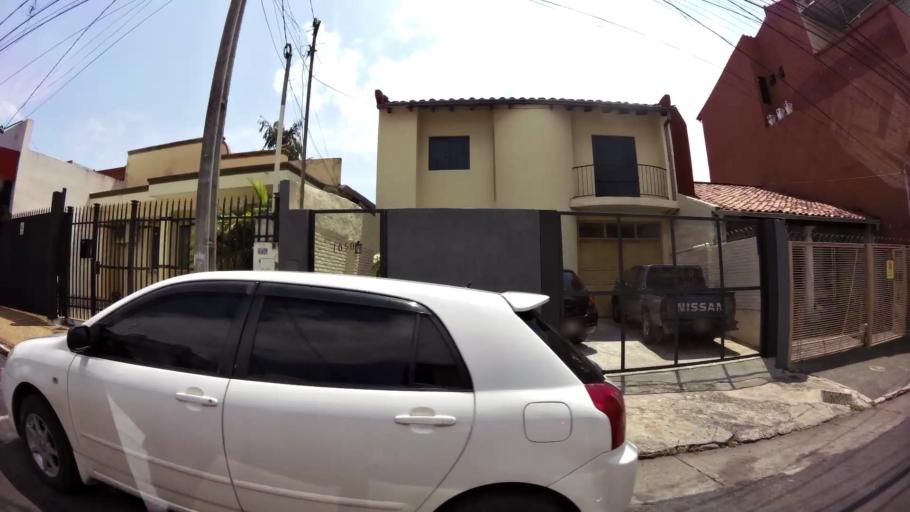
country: PY
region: Asuncion
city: Asuncion
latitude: -25.2913
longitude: -57.6344
